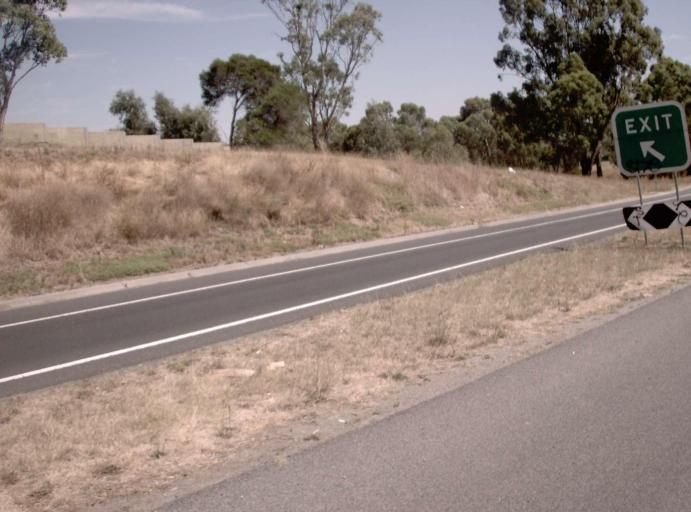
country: AU
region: Victoria
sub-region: Casey
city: Doveton
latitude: -37.9745
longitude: 145.2379
